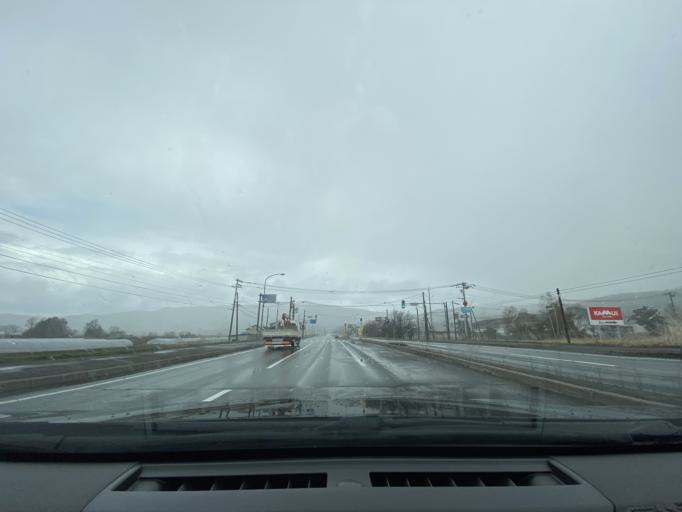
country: JP
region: Hokkaido
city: Fukagawa
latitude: 43.7190
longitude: 142.1818
